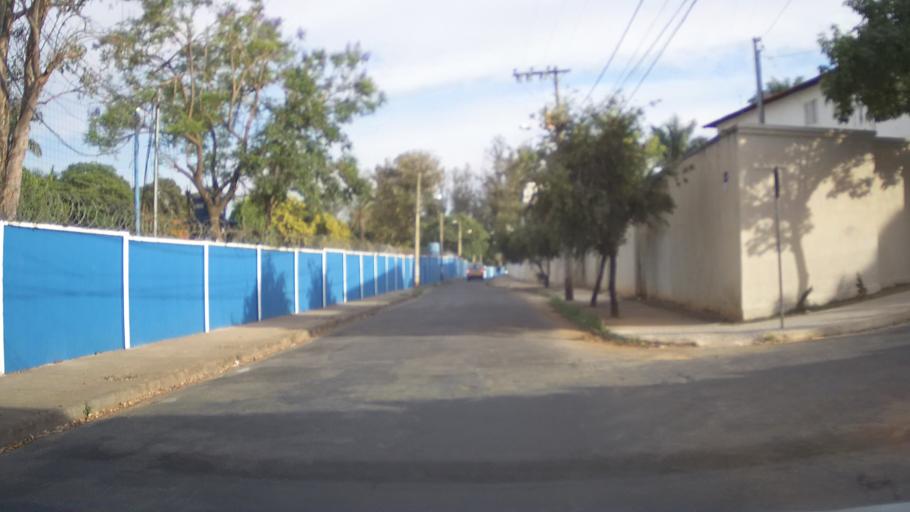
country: BR
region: Minas Gerais
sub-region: Belo Horizonte
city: Belo Horizonte
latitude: -19.8635
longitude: -43.9963
